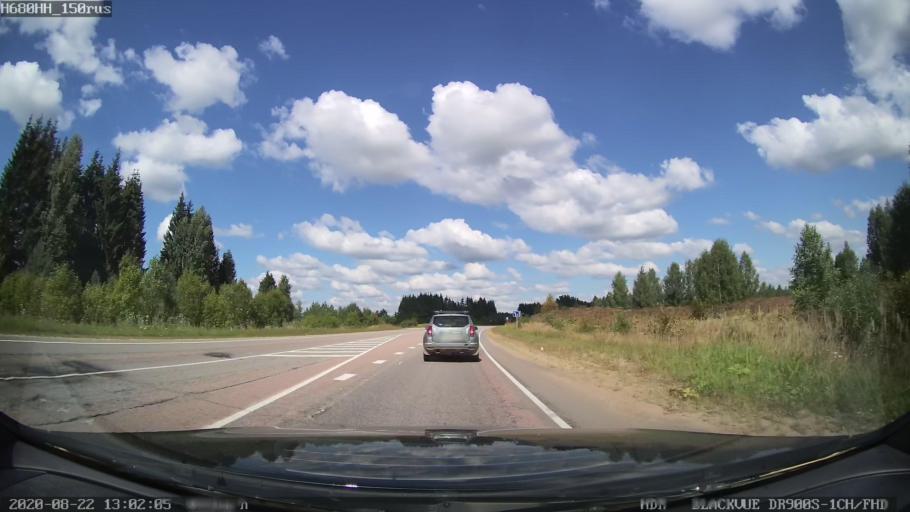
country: RU
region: Tverskaya
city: Bezhetsk
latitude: 57.6445
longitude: 36.3947
